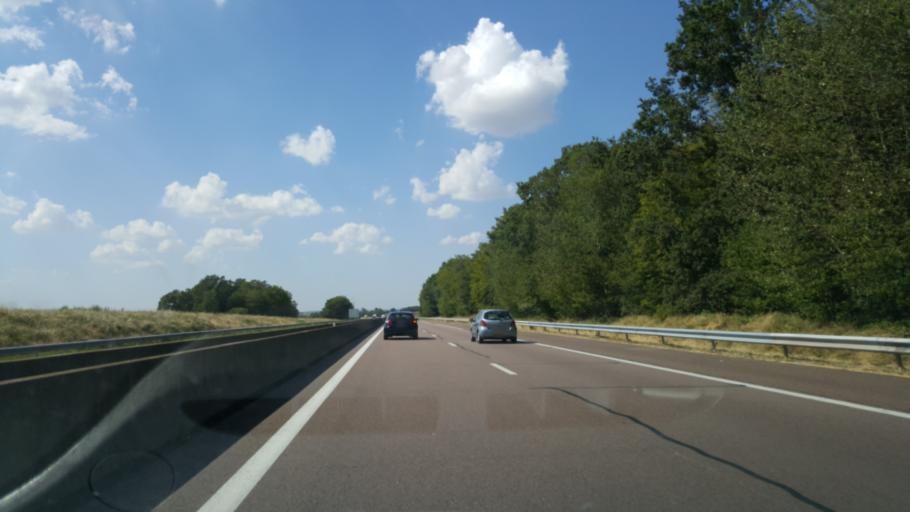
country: FR
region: Bourgogne
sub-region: Departement de la Cote-d'Or
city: Semur-en-Auxois
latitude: 47.4607
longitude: 4.2540
